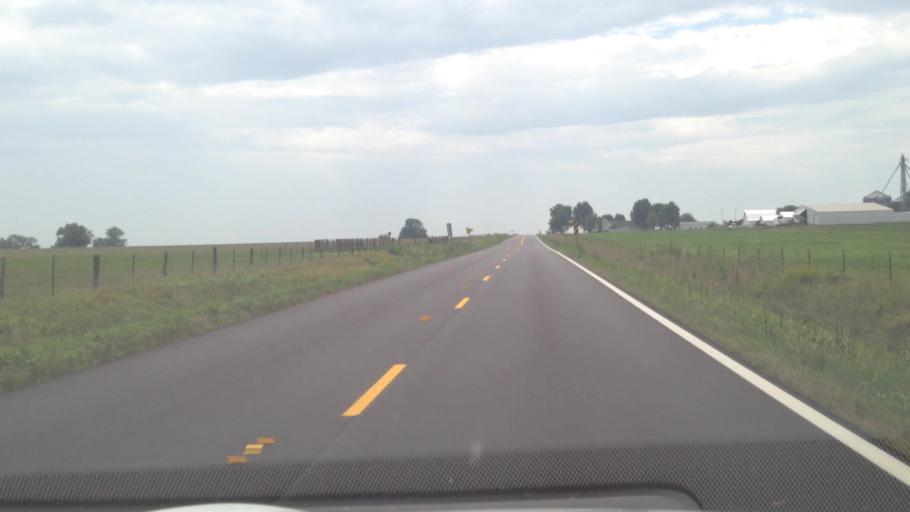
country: US
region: Kansas
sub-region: Crawford County
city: Girard
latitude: 37.5499
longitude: -94.9605
